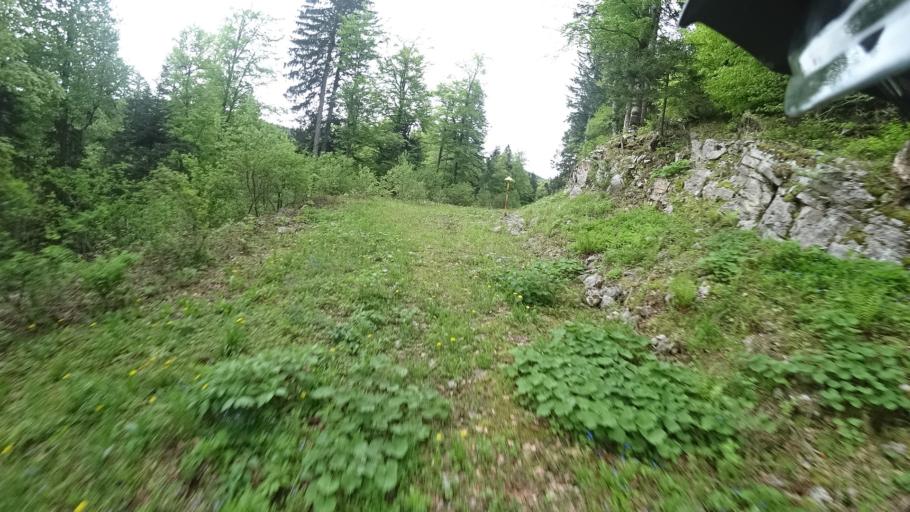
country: HR
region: Karlovacka
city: Plaski
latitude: 44.9597
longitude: 15.4113
